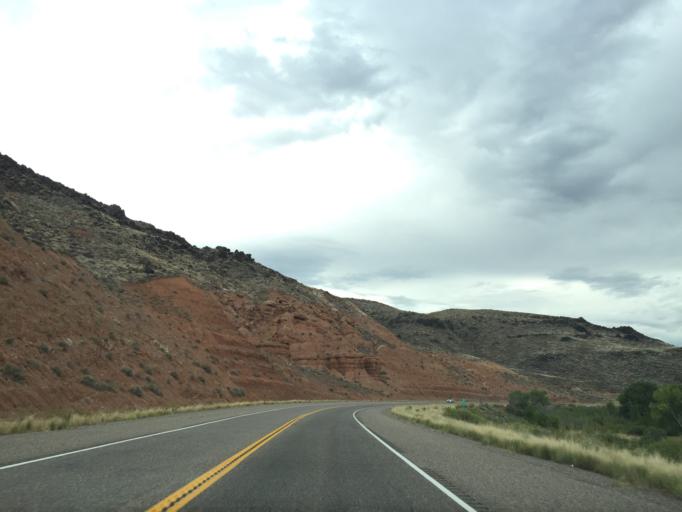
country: US
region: Utah
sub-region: Washington County
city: LaVerkin
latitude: 37.1789
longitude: -113.1194
